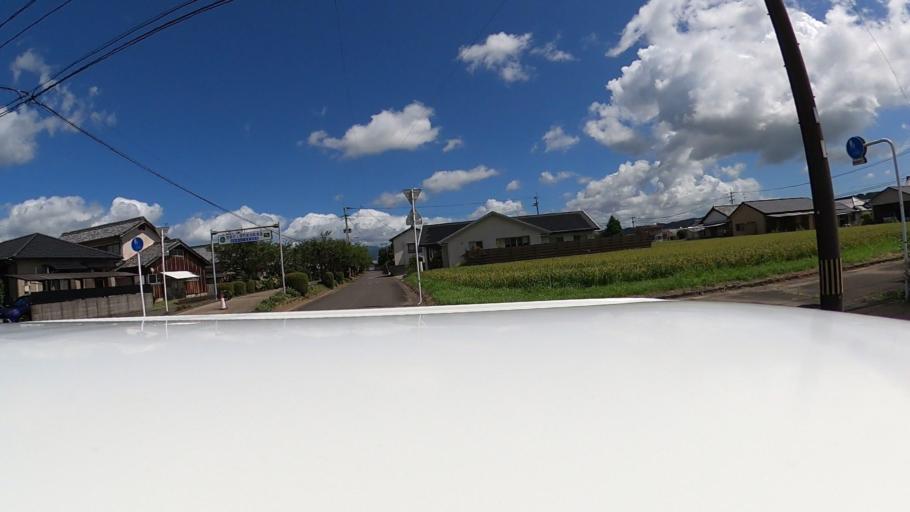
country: JP
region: Miyazaki
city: Tsuma
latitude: 32.1009
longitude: 131.4069
